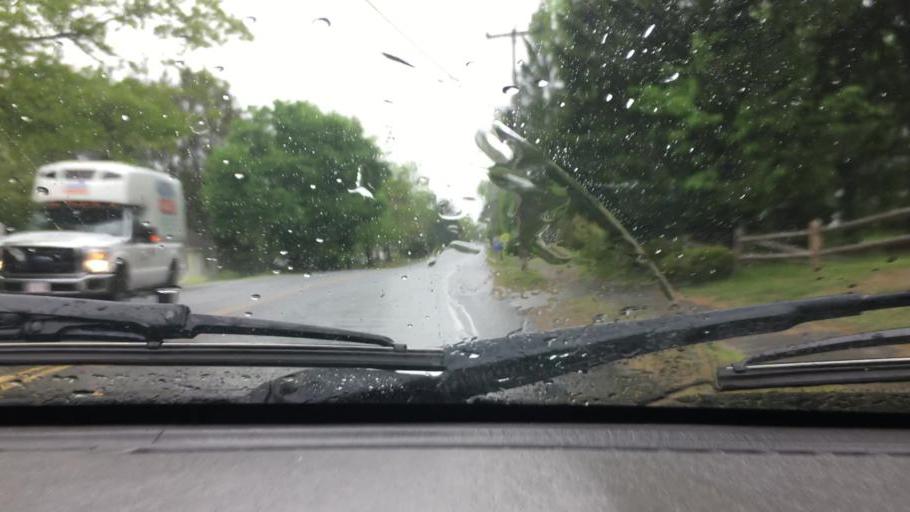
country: US
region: Massachusetts
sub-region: Franklin County
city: Turners Falls
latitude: 42.5889
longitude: -72.5386
